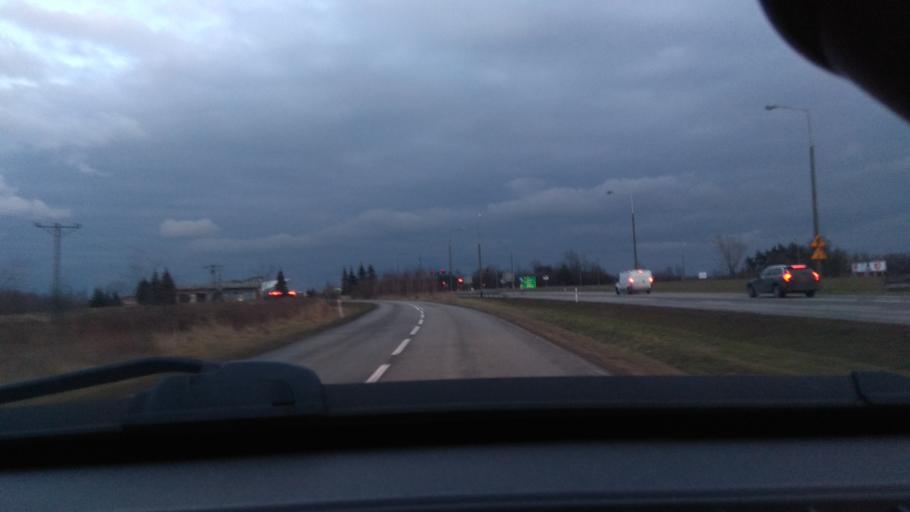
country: PL
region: Greater Poland Voivodeship
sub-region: Powiat kepinski
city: Kepno
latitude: 51.2881
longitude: 18.0116
